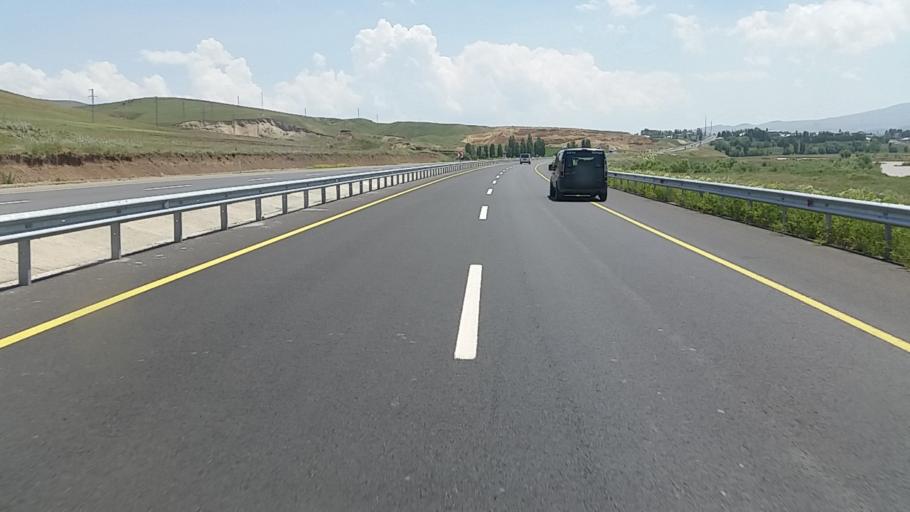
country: TR
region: Agri
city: Taslicay
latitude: 39.6525
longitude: 43.3577
